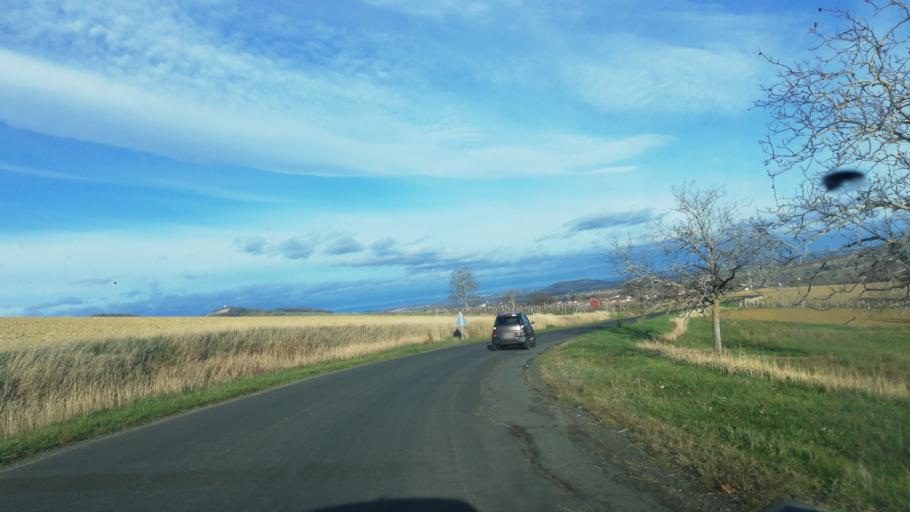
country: FR
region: Auvergne
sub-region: Departement du Puy-de-Dome
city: Billom
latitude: 45.7042
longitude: 3.3517
